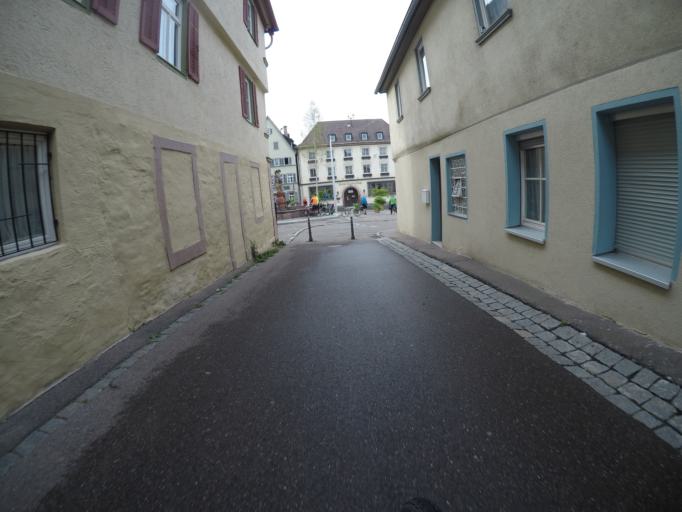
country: DE
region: Baden-Wuerttemberg
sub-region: Regierungsbezirk Stuttgart
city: Weil der Stadt
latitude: 48.7503
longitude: 8.8703
